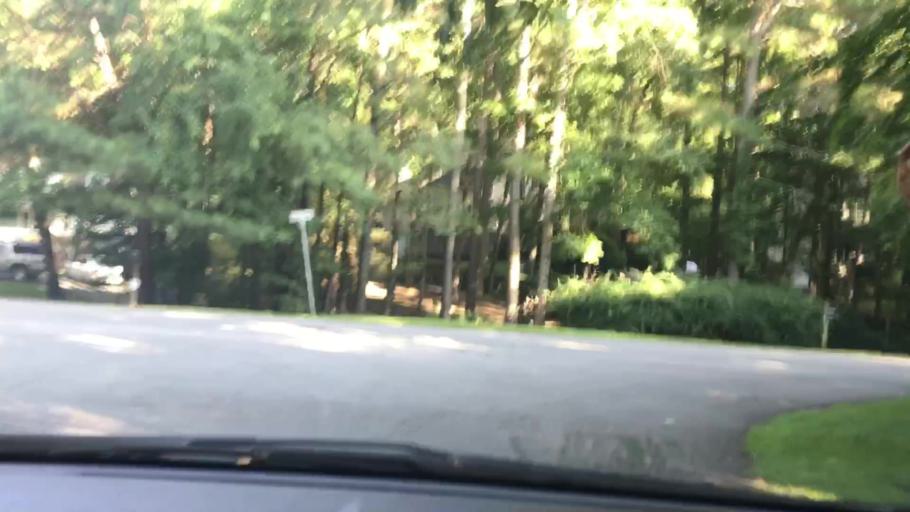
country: US
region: Virginia
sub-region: Henrico County
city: Short Pump
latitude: 37.6084
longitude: -77.7155
